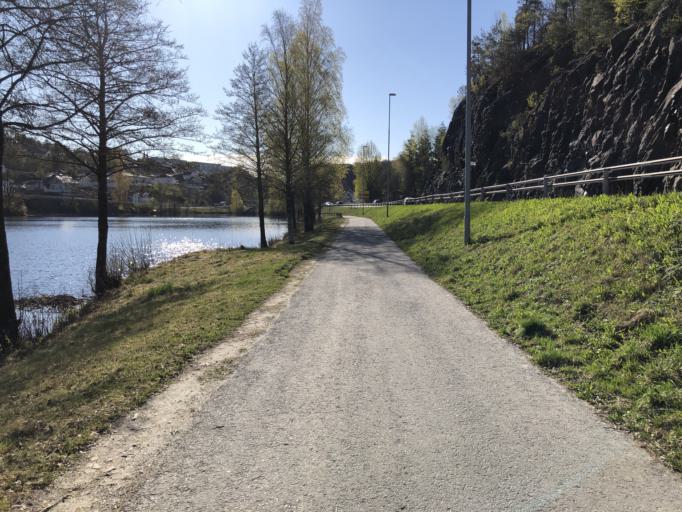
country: NO
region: Aust-Agder
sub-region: Arendal
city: Arendal
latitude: 58.4727
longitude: 8.7538
